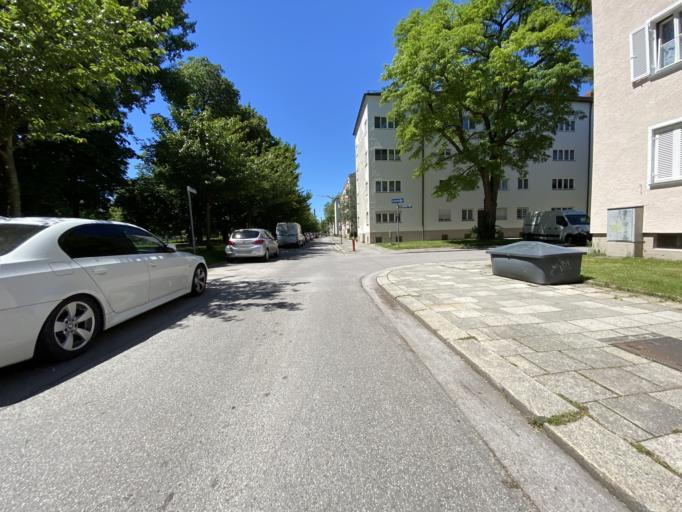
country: DE
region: Bavaria
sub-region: Upper Bavaria
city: Bogenhausen
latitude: 48.1232
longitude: 11.6163
